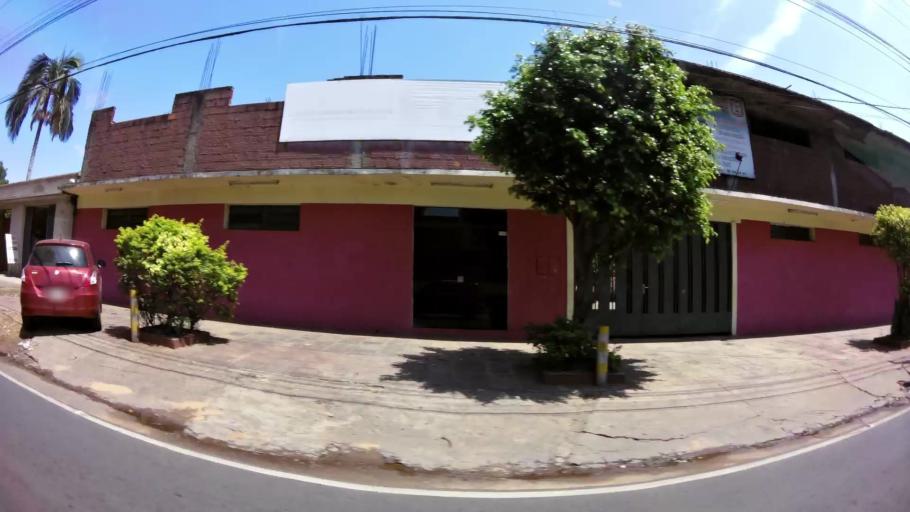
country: PY
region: Central
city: San Lorenzo
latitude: -25.3537
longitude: -57.5135
